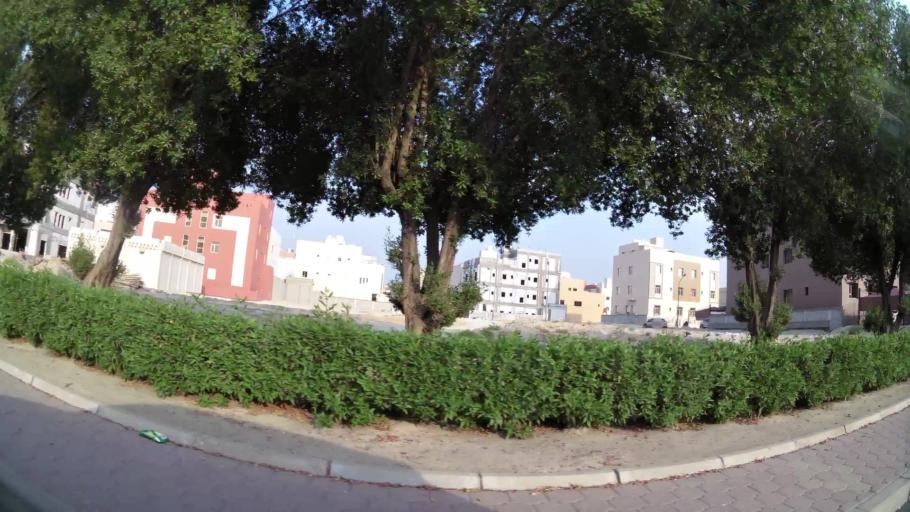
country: KW
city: Al Funaytis
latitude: 29.2321
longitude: 48.0847
